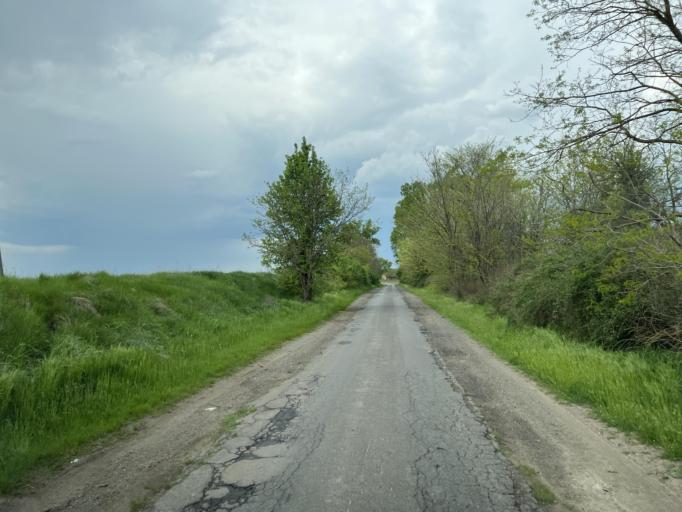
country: HU
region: Pest
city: Nagykoros
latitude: 46.9980
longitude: 19.8006
